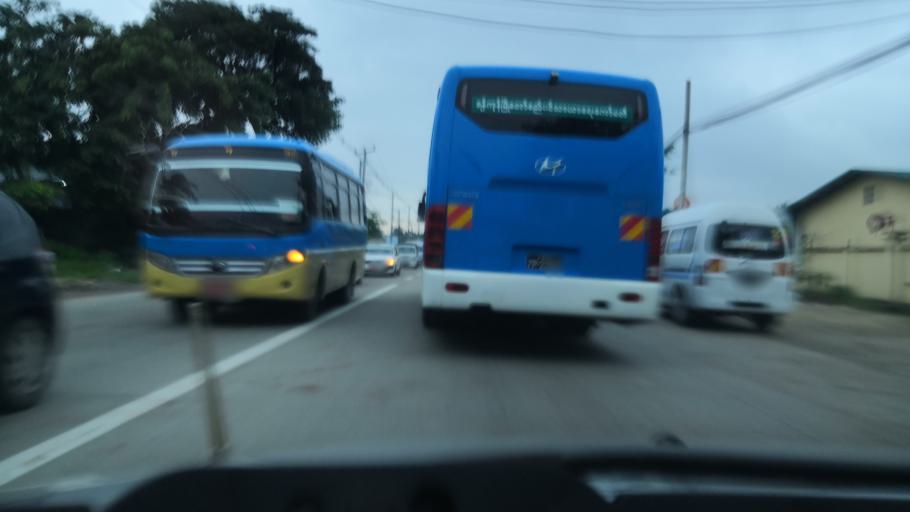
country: MM
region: Yangon
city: Yangon
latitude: 16.8854
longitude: 96.1675
